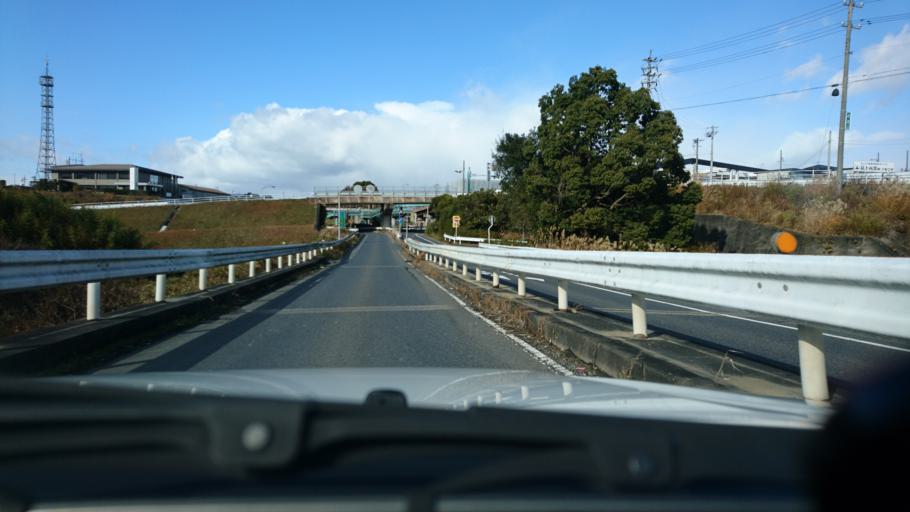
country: JP
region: Mie
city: Ueno-ebisumachi
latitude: 34.7534
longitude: 136.1477
